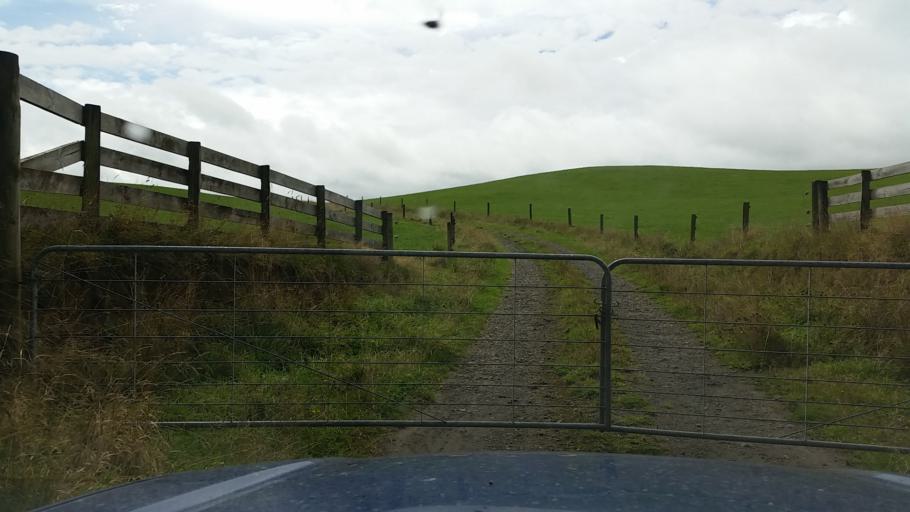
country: NZ
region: Taranaki
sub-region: South Taranaki District
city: Eltham
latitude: -39.3352
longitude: 174.4283
